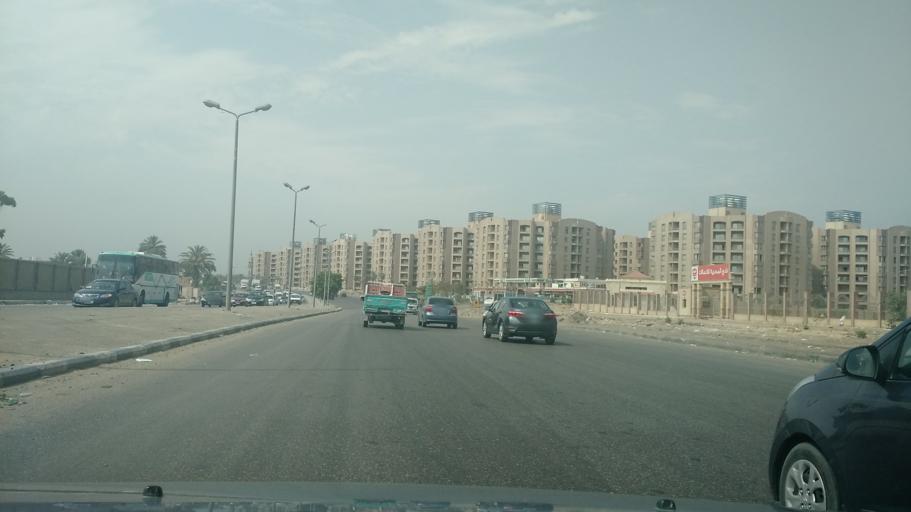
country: EG
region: Al Jizah
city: Al Hawamidiyah
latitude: 29.9697
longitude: 31.2888
